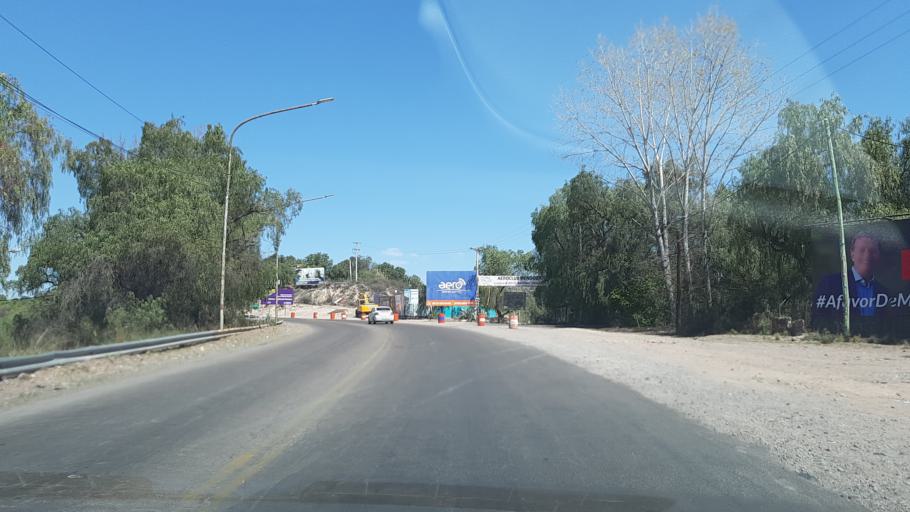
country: AR
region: Mendoza
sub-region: Departamento de Godoy Cruz
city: Godoy Cruz
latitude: -32.9635
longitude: -68.8707
